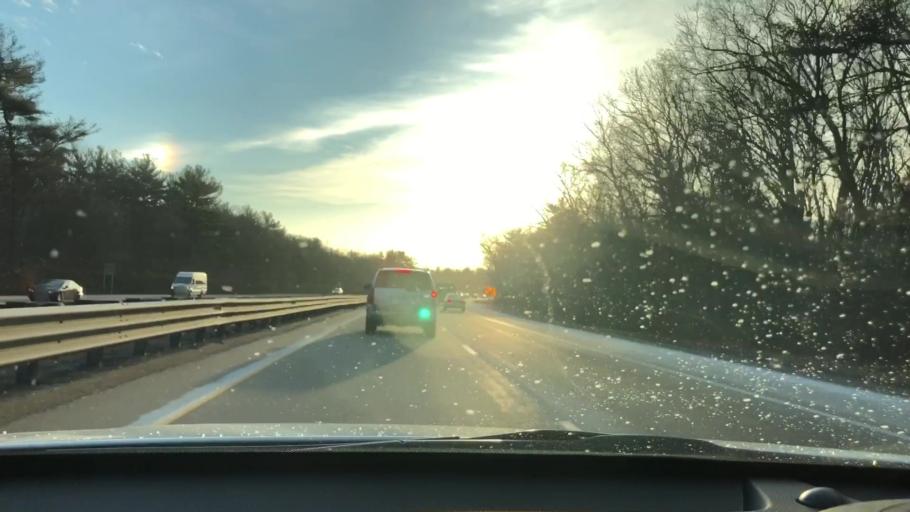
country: US
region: Massachusetts
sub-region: Norfolk County
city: Weymouth
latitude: 42.1828
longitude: -70.9221
